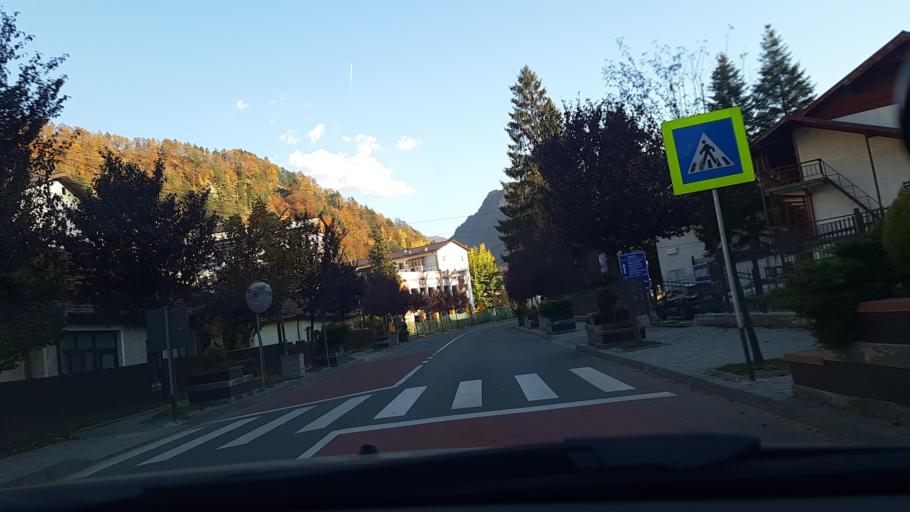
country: RO
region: Valcea
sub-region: Comuna Brezoi
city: Brezoi
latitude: 45.3433
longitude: 24.2450
